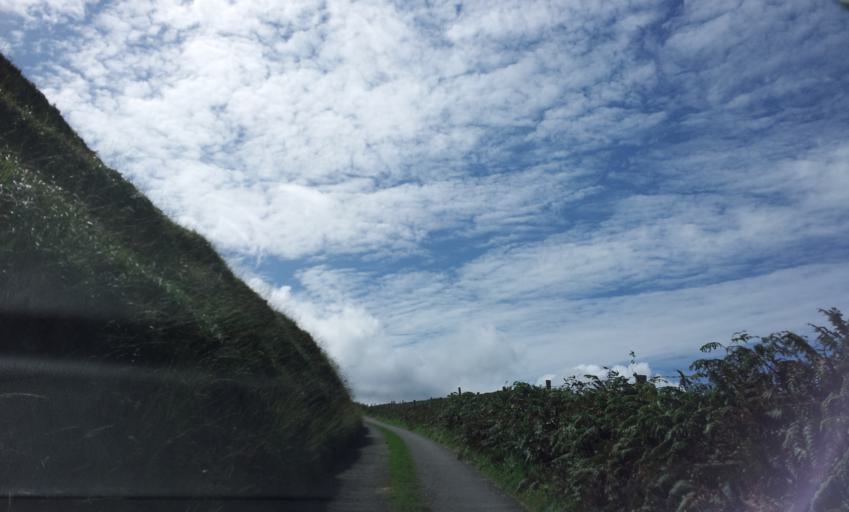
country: IE
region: Munster
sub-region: Ciarrai
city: Killorglin
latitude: 52.0486
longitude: -9.9862
